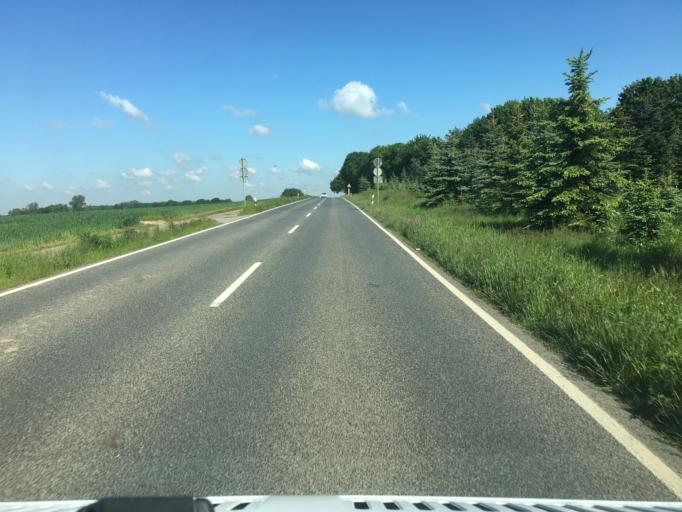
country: DE
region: North Rhine-Westphalia
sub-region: Regierungsbezirk Koln
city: Linnich
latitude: 50.9682
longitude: 6.3159
